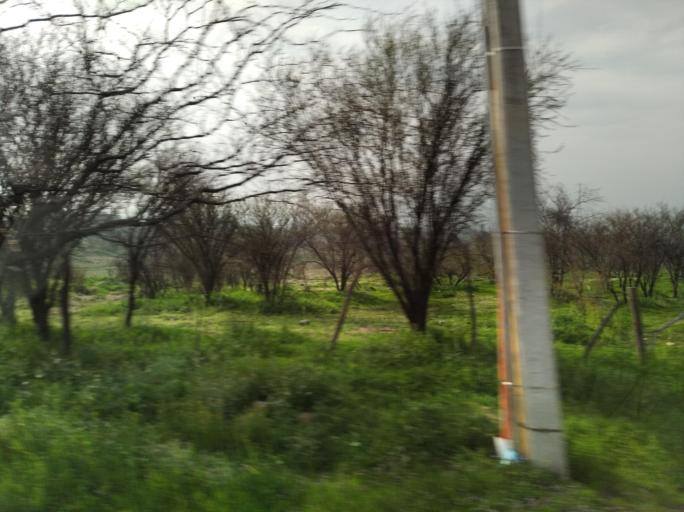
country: CL
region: Santiago Metropolitan
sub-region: Provincia de Chacabuco
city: Lampa
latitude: -33.1772
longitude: -70.8950
